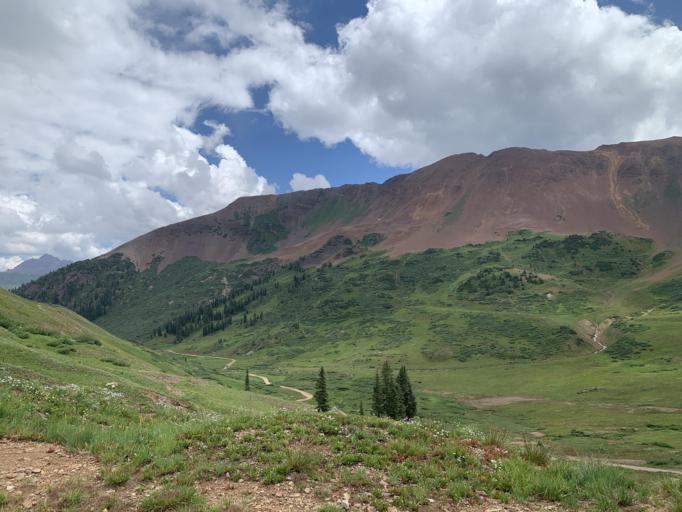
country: US
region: Colorado
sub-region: Gunnison County
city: Crested Butte
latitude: 38.9910
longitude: -107.0656
